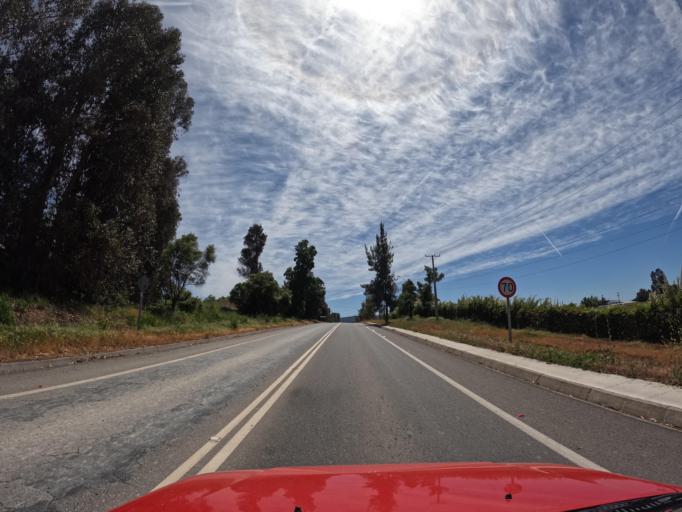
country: CL
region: Maule
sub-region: Provincia de Talca
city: Talca
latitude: -35.2991
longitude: -71.5255
